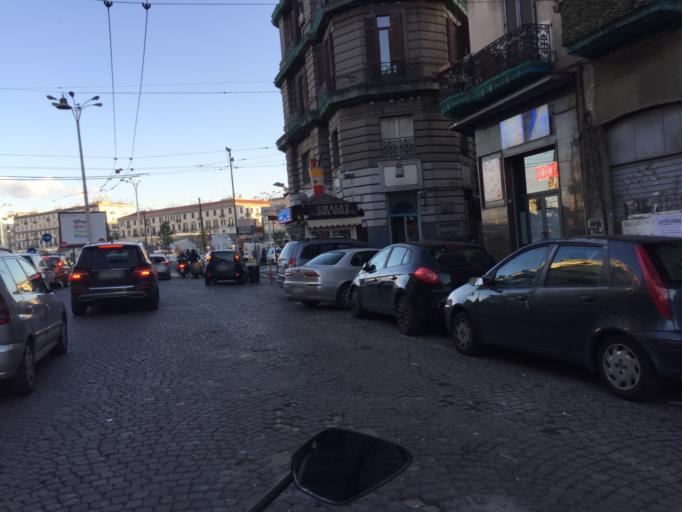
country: IT
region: Campania
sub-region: Provincia di Napoli
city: Napoli
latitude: 40.8530
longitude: 14.2669
